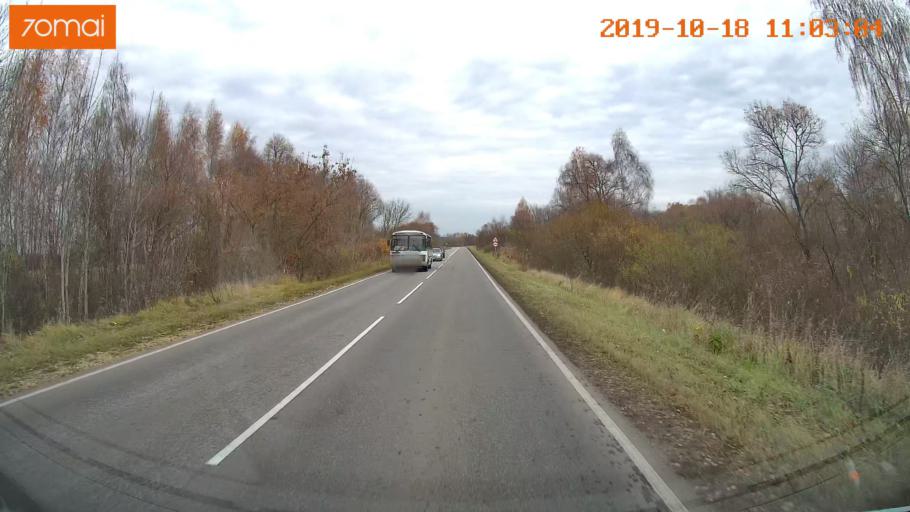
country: RU
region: Tula
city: Yepifan'
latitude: 53.8745
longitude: 38.5461
